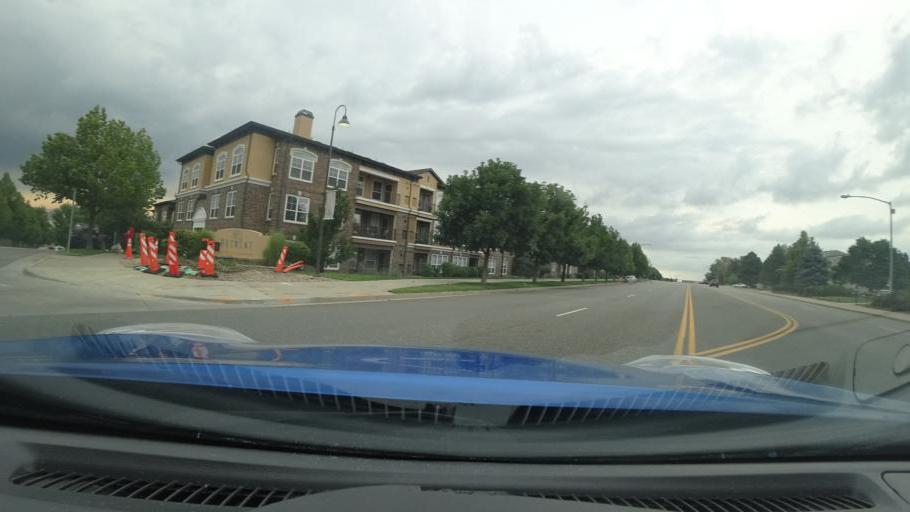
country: US
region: Colorado
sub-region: Adams County
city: Aurora
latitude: 39.6994
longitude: -104.8193
